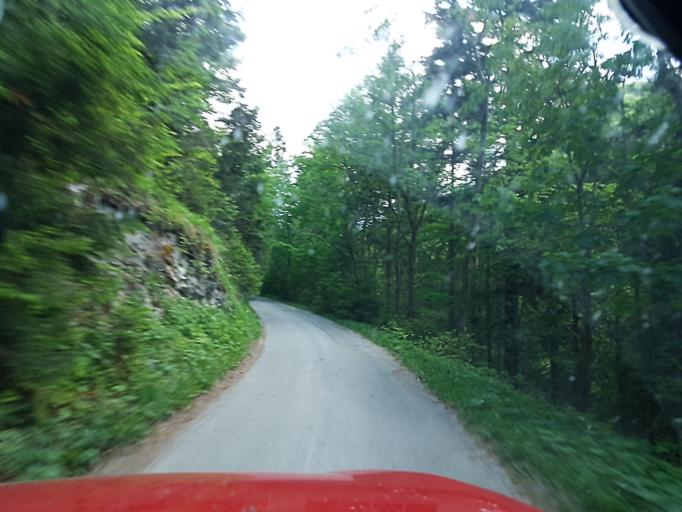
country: SK
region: Zilinsky
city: Ruzomberok
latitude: 49.0553
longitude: 19.2759
